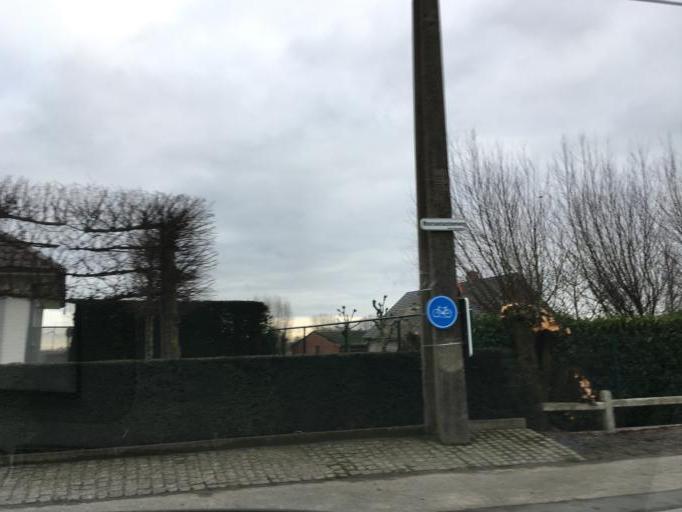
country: BE
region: Flanders
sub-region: Provincie West-Vlaanderen
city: Ledegem
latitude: 50.8884
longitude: 3.1478
